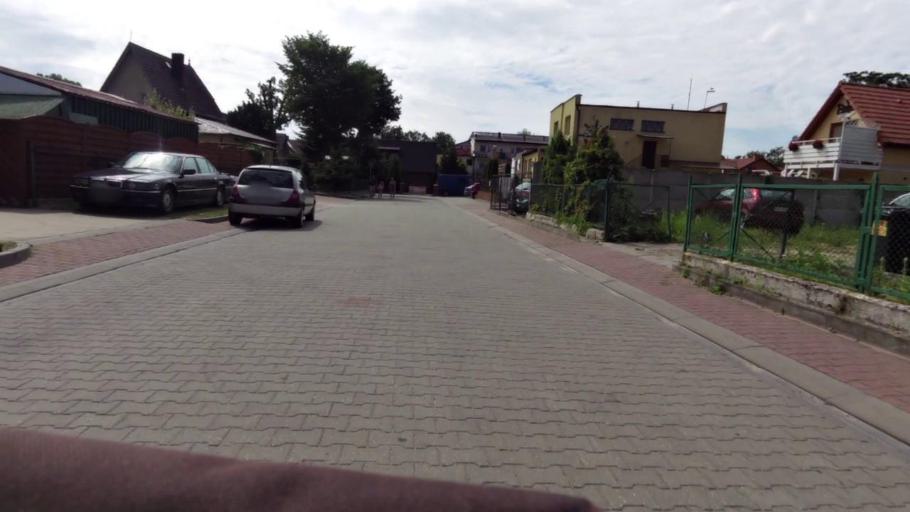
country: PL
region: West Pomeranian Voivodeship
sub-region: Powiat kamienski
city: Dziwnow
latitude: 54.0224
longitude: 14.7415
